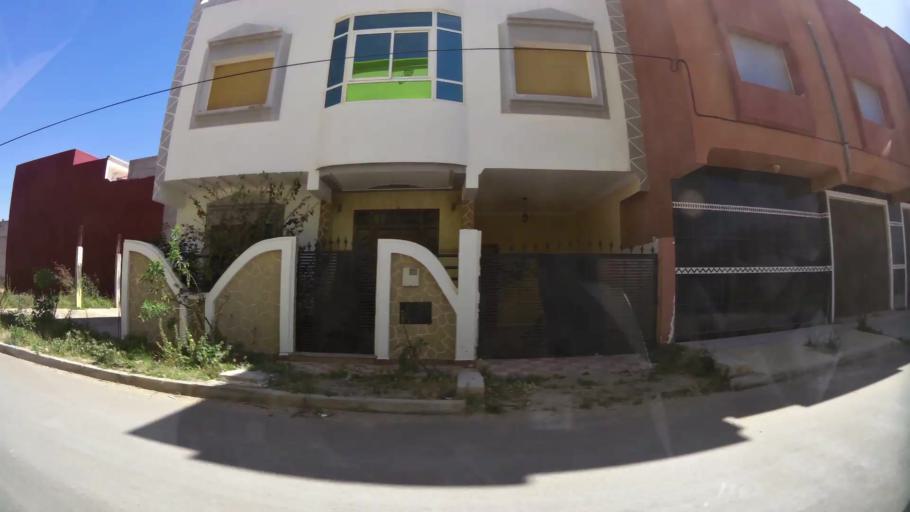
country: MA
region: Oriental
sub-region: Berkane-Taourirt
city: Madagh
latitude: 35.1367
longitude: -2.4261
